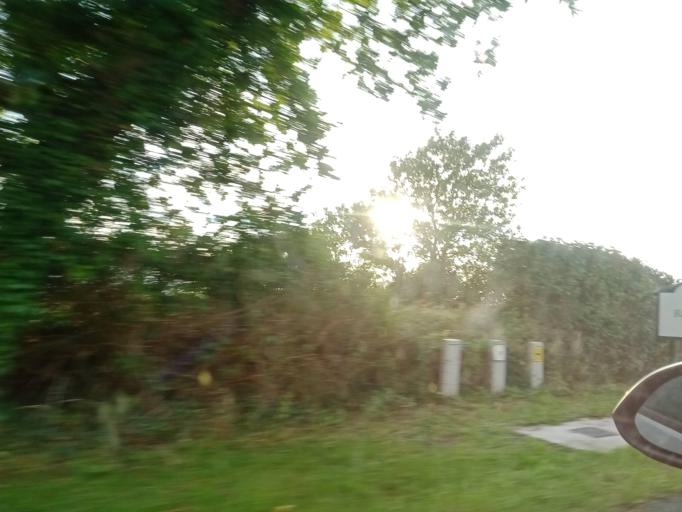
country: IE
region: Leinster
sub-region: Laois
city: Stradbally
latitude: 53.0057
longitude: -7.2140
